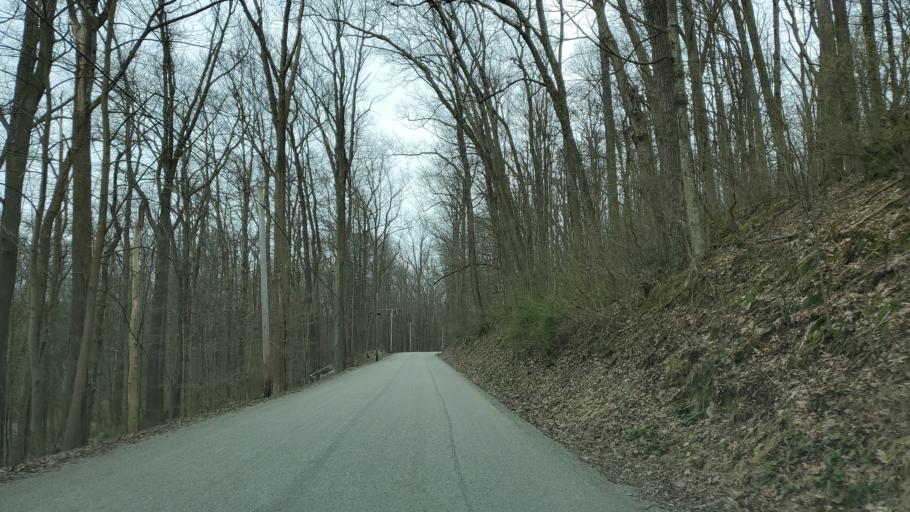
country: US
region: Pennsylvania
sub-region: Westmoreland County
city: Ligonier
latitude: 40.1816
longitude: -79.2390
